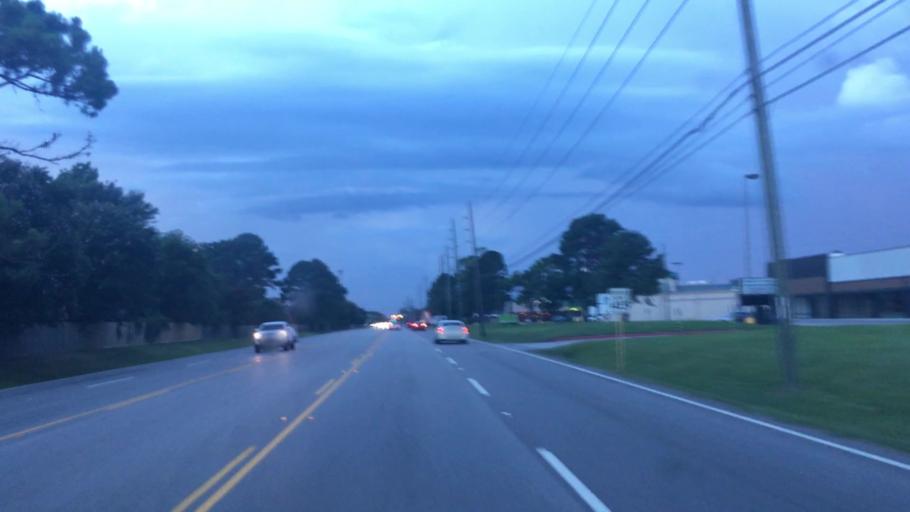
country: US
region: Texas
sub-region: Harris County
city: Atascocita
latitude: 29.9964
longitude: -95.1688
